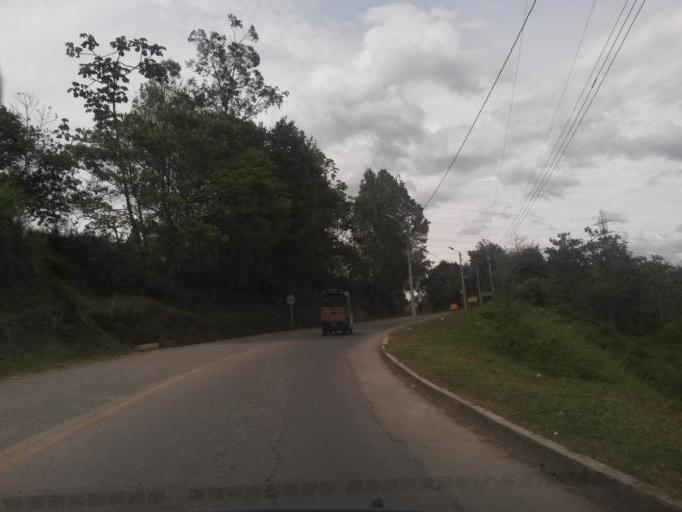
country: CO
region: Cauca
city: Popayan
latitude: 2.4571
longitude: -76.6480
